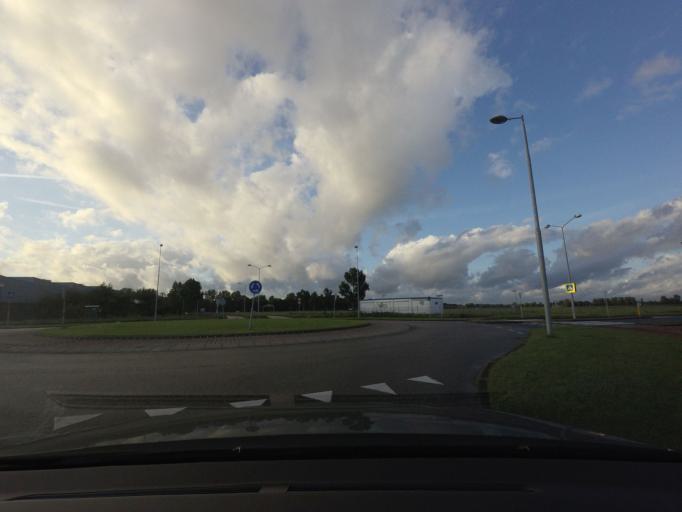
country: NL
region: North Holland
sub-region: Gemeente Alkmaar
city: Alkmaar
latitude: 52.6550
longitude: 4.7719
